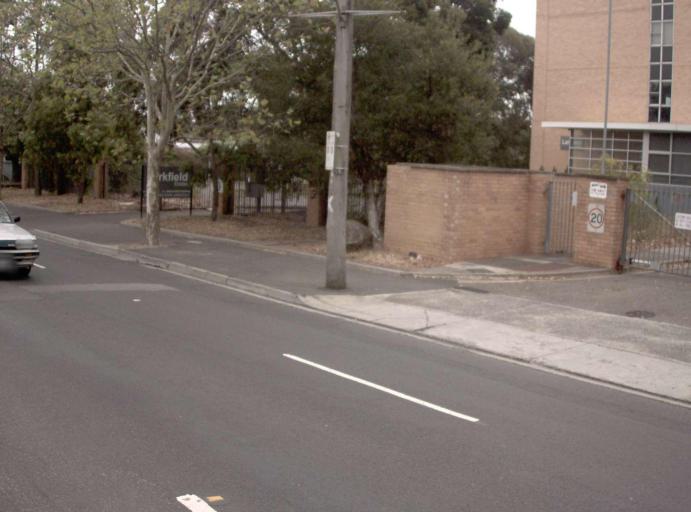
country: AU
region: Victoria
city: Toorak
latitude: -37.8518
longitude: 145.0119
